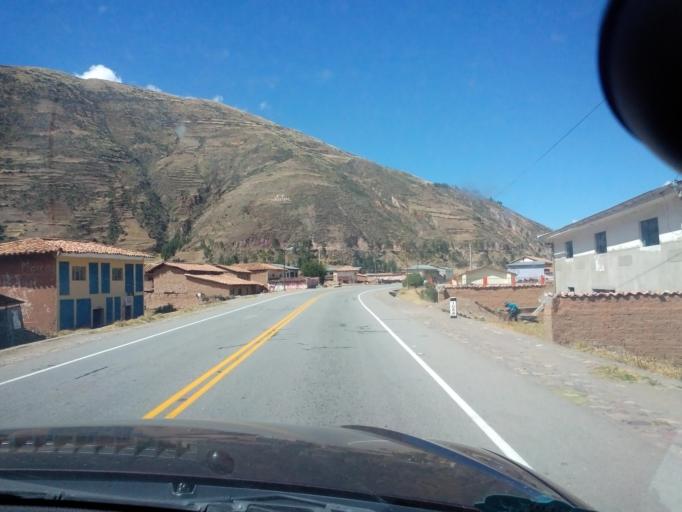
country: PE
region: Cusco
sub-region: Provincia de Canchis
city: Checacupe
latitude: -13.9936
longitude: -71.4625
